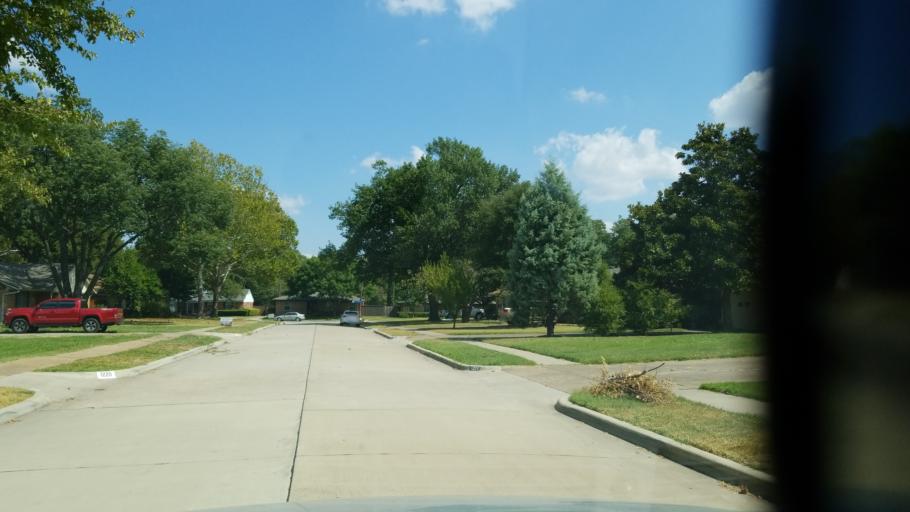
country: US
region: Texas
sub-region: Dallas County
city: Richardson
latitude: 32.9609
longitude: -96.7602
